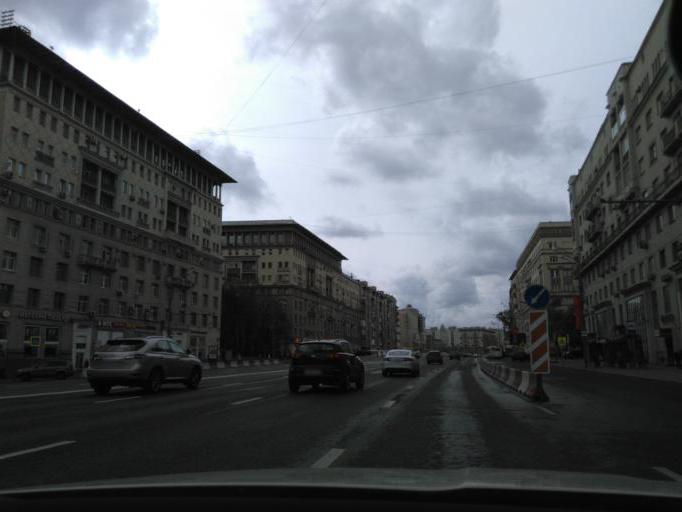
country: RU
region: Moscow
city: Taganskiy
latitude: 55.7615
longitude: 37.6573
